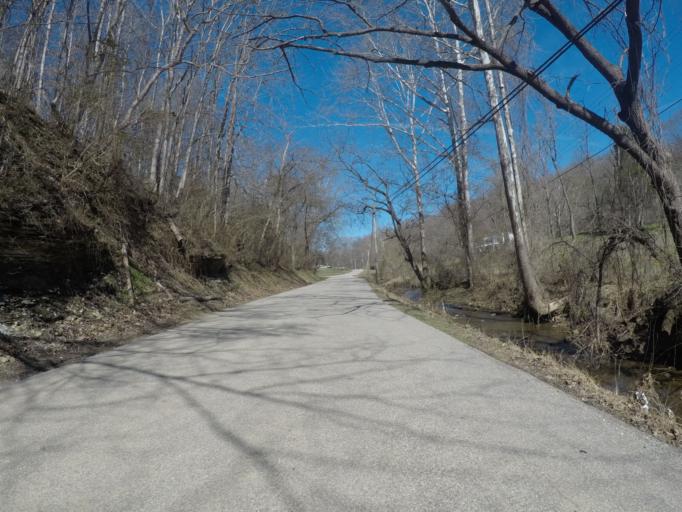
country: US
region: Ohio
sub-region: Lawrence County
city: Burlington
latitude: 38.4479
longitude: -82.5037
